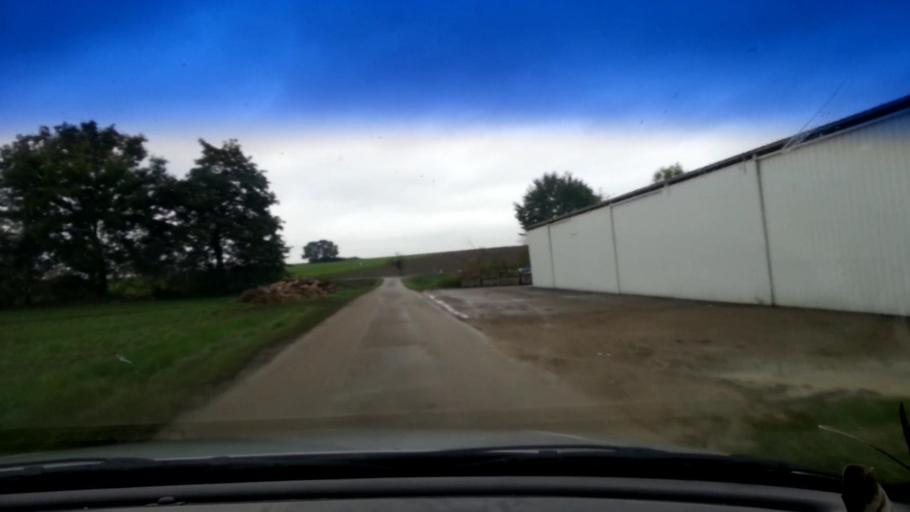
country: DE
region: Bavaria
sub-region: Upper Franconia
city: Litzendorf
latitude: 49.9384
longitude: 11.0046
